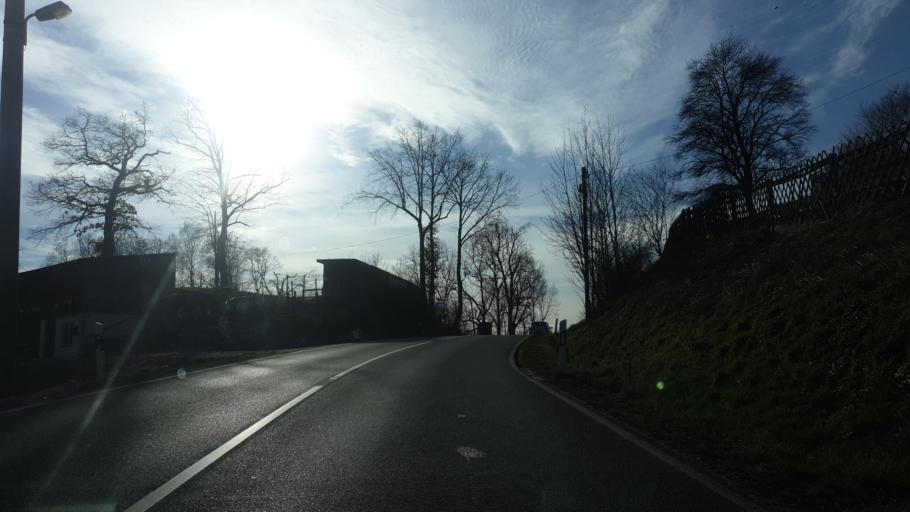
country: DE
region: Saxony
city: Hartenstein
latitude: 50.6661
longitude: 12.6423
